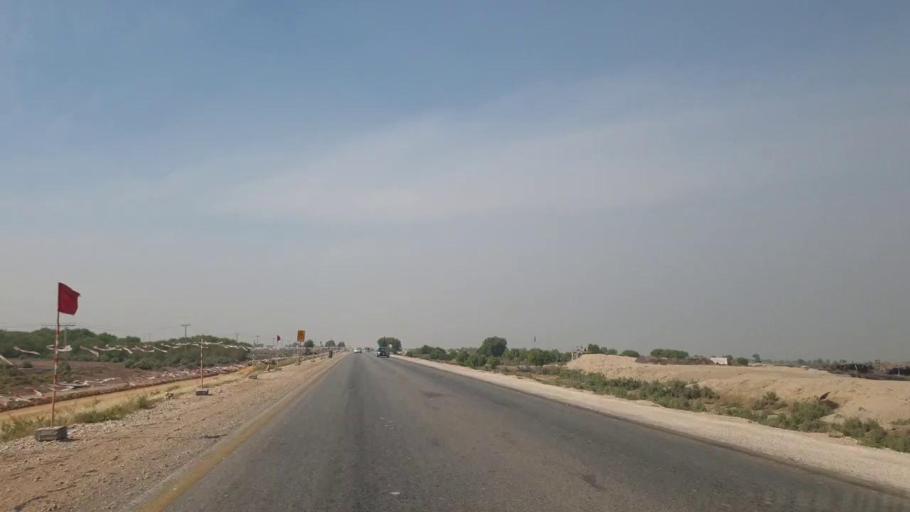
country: PK
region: Sindh
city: Sann
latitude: 25.9945
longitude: 68.1704
